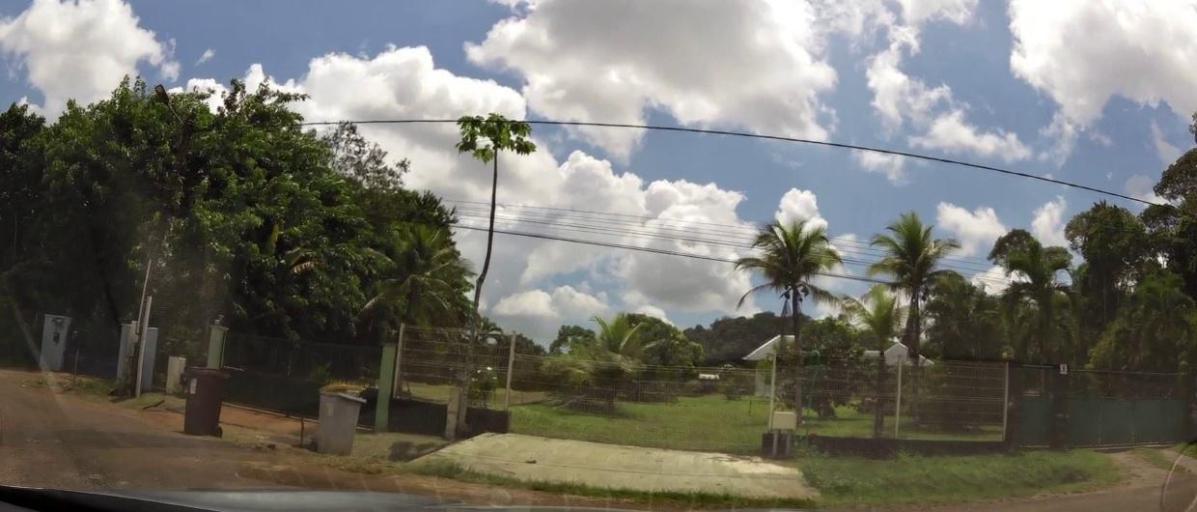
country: GF
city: Macouria
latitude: 4.8785
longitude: -52.3593
